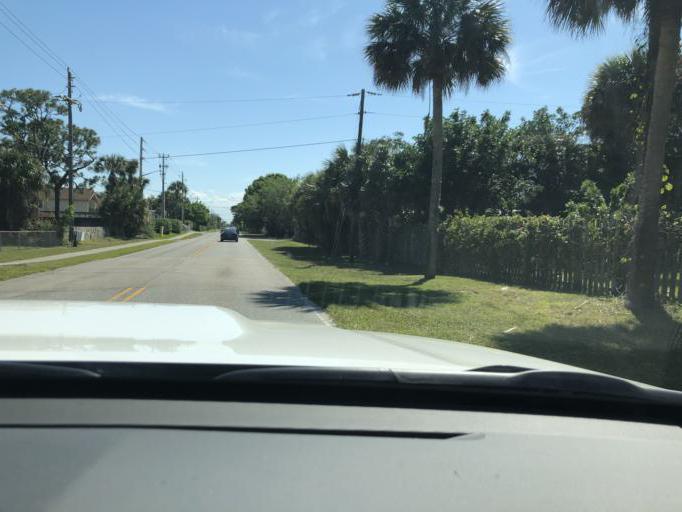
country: US
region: Florida
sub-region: Martin County
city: Stuart
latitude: 27.1838
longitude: -80.2571
